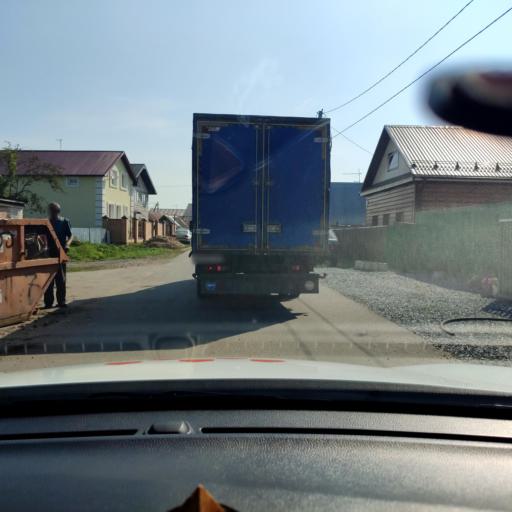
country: RU
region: Tatarstan
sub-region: Gorod Kazan'
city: Kazan
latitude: 55.7253
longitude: 49.1434
